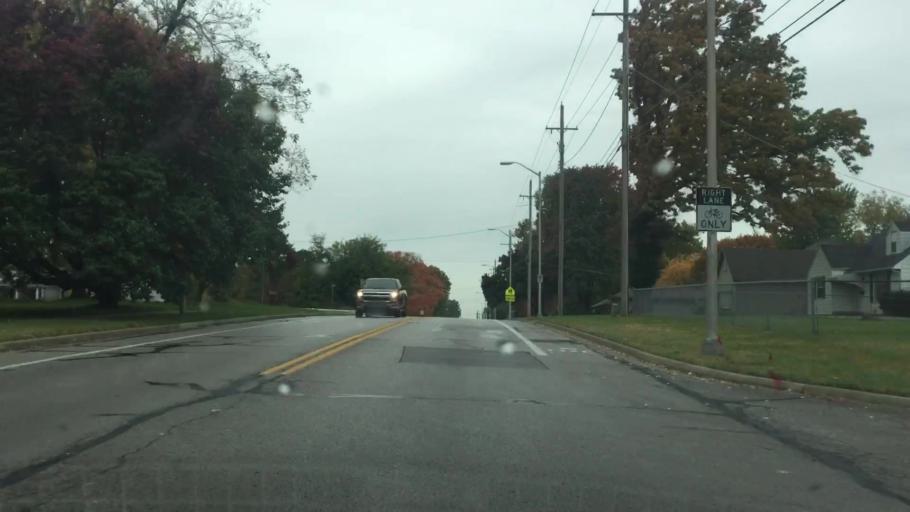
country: US
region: Kansas
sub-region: Johnson County
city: Shawnee
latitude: 39.0293
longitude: -94.7298
